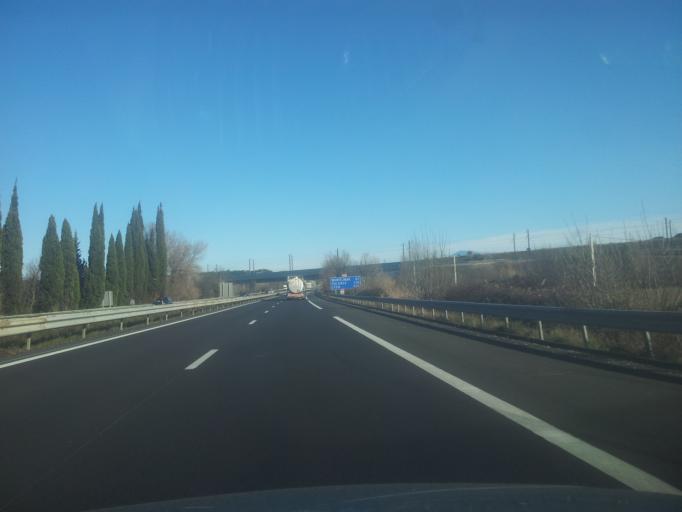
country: FR
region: Languedoc-Roussillon
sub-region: Departement du Gard
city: Pujaut
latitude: 44.0260
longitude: 4.7427
